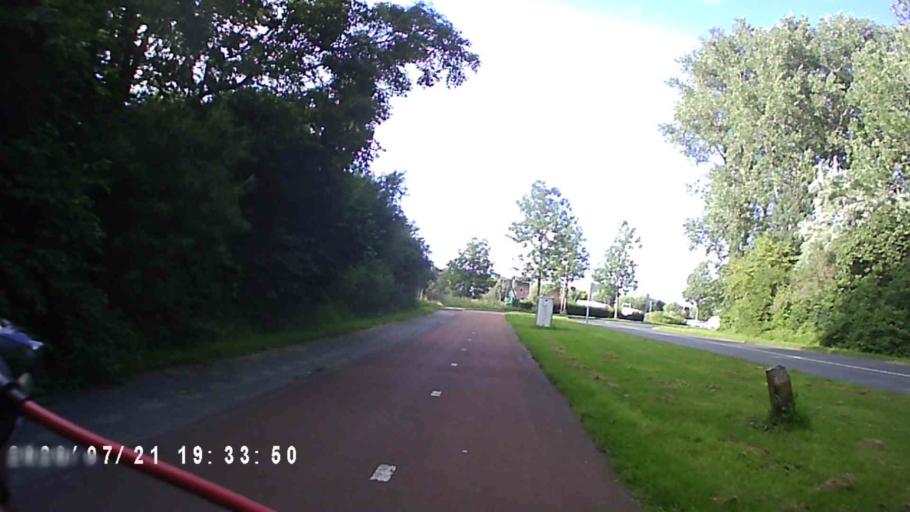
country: NL
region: Groningen
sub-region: Gemeente Groningen
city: Oosterpark
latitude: 53.2399
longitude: 6.6140
